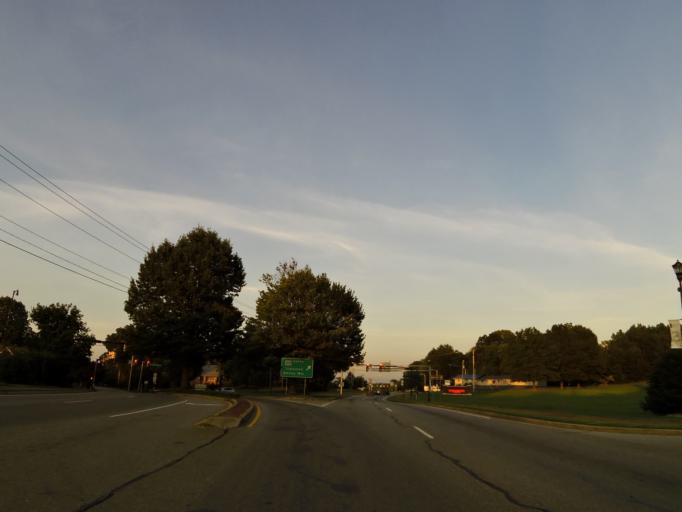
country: US
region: Tennessee
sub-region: Blount County
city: Maryville
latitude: 35.7552
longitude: -83.9639
